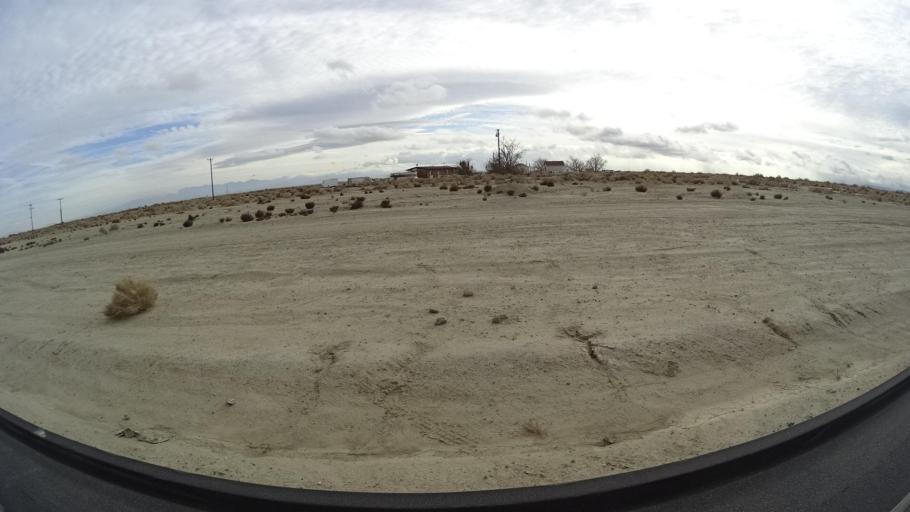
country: US
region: California
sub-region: Kern County
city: Rosamond
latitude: 34.8495
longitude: -118.1868
